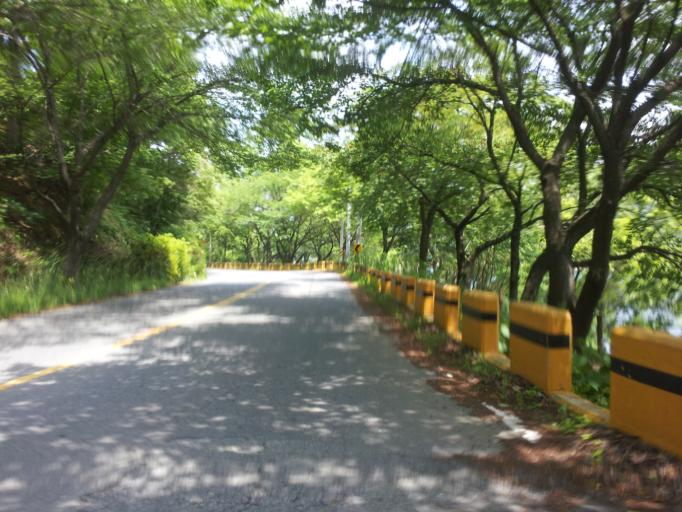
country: KR
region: Daejeon
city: Sintansin
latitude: 36.4362
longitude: 127.4712
